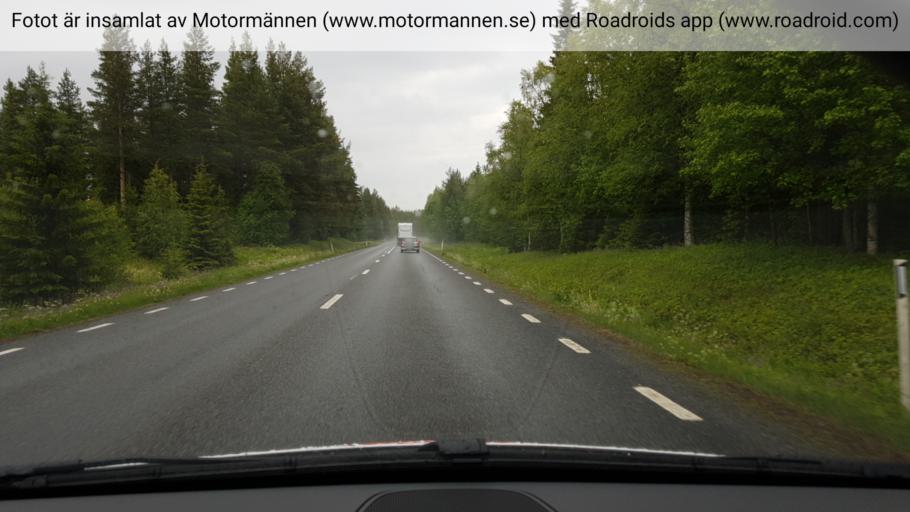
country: SE
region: Jaemtland
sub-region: Stroemsunds Kommun
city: Stroemsund
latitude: 63.5292
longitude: 15.3283
